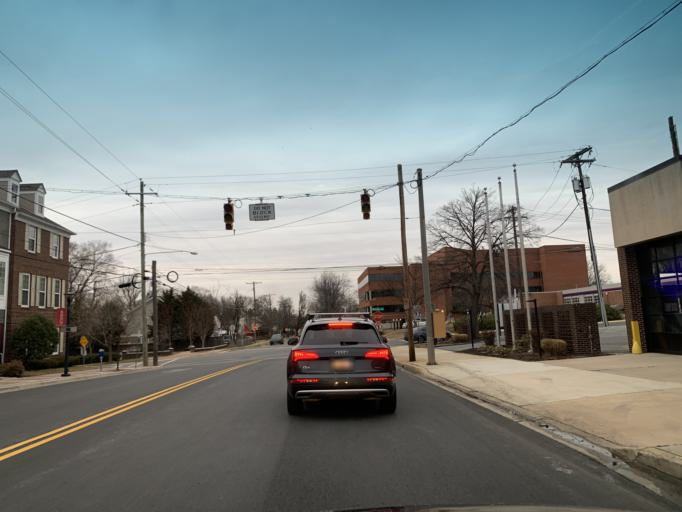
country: US
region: Maryland
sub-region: Montgomery County
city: Wheaton
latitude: 39.0426
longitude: -77.0532
